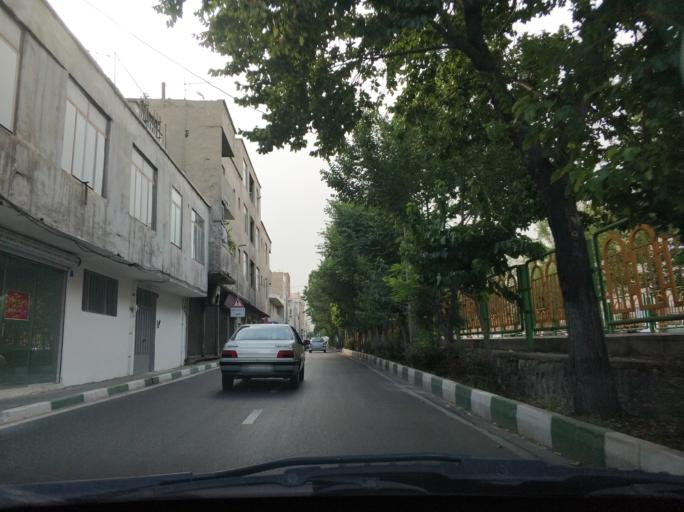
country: IR
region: Tehran
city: Tehran
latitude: 35.7145
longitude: 51.4828
